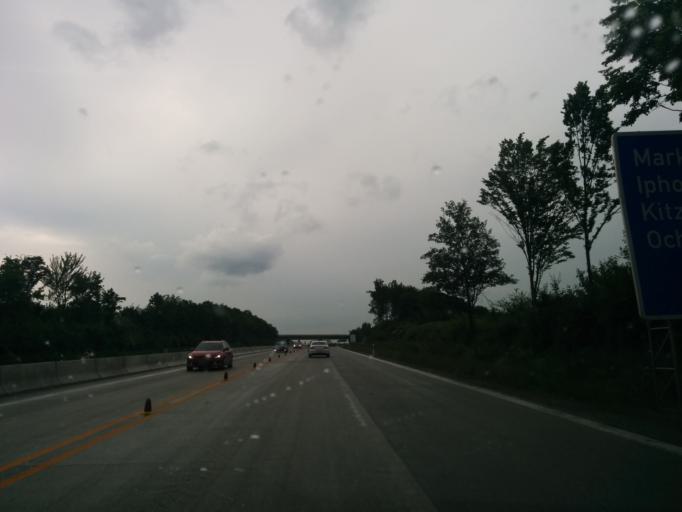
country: DE
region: Bavaria
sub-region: Regierungsbezirk Unterfranken
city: Marktbreit
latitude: 49.6489
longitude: 10.1496
